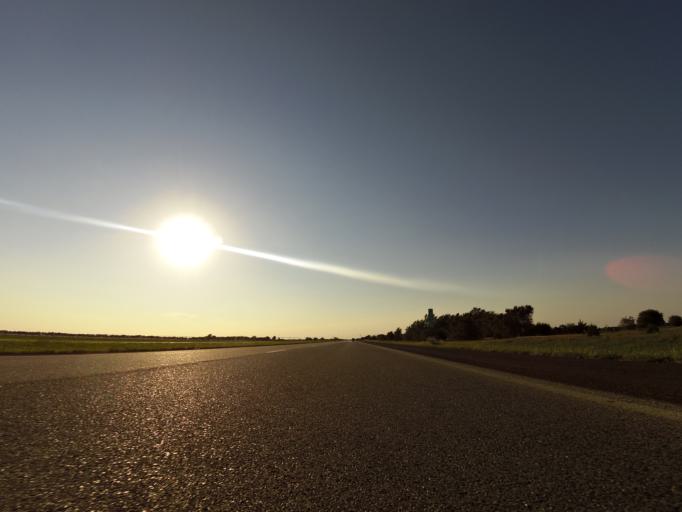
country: US
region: Kansas
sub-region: Reno County
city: South Hutchinson
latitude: 37.9511
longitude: -97.8935
